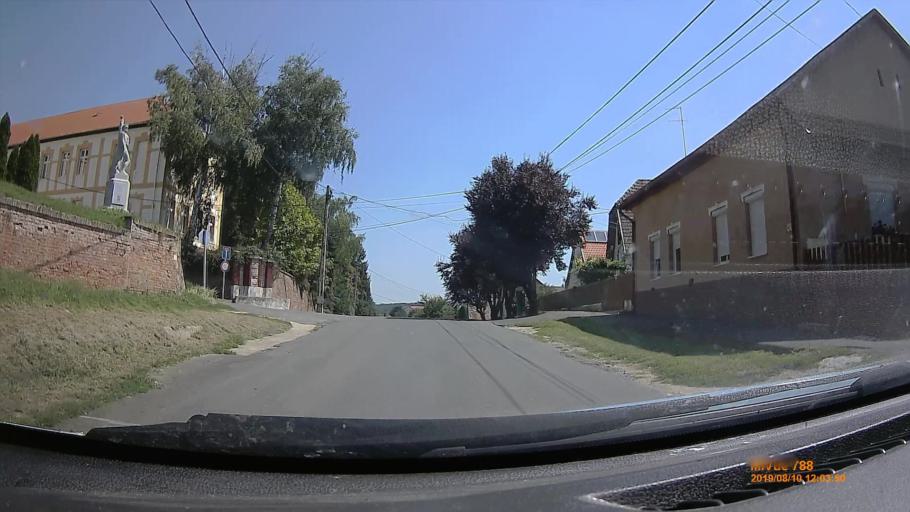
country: HU
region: Somogy
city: Somogyvar
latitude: 46.5796
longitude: 17.6544
